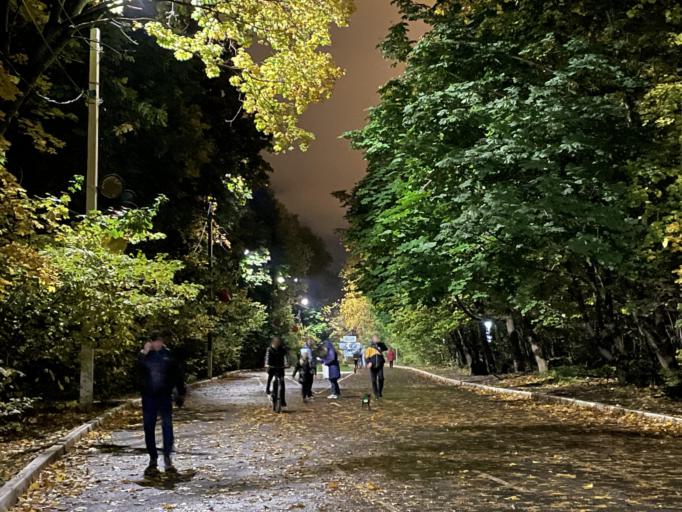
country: RU
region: Chuvashia
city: Novocheboksarsk
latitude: 56.1215
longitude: 47.4757
